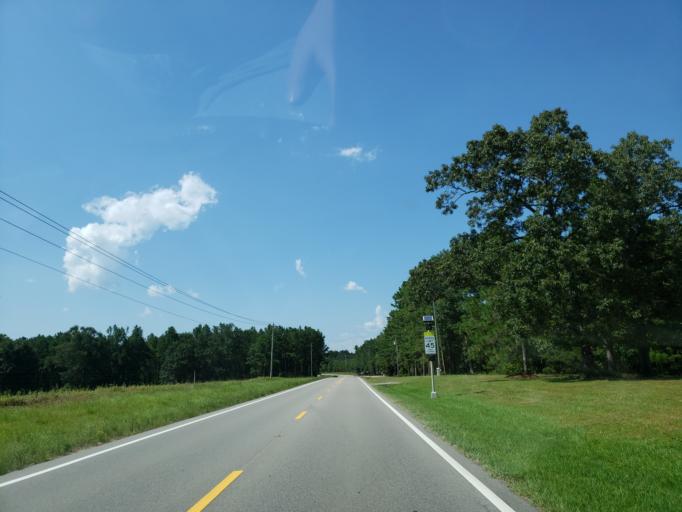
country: US
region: Mississippi
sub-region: Lamar County
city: Sumrall
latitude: 31.3593
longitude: -89.4981
